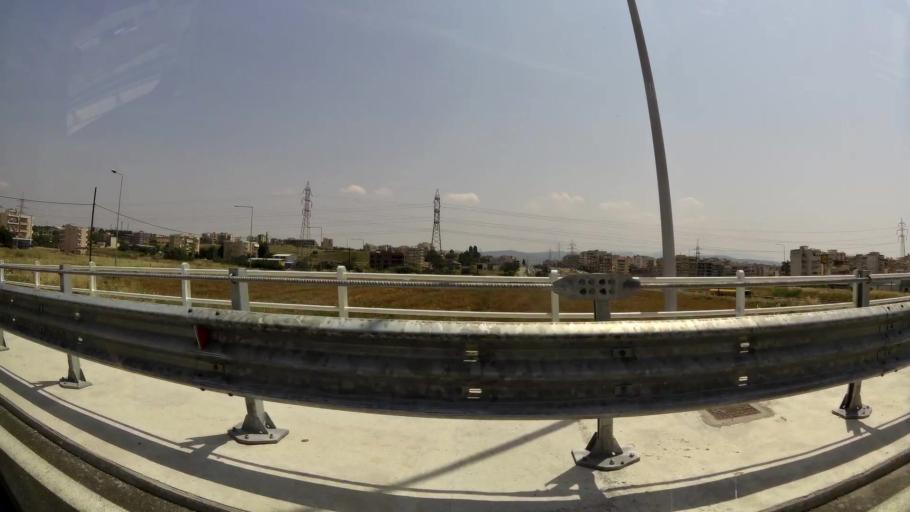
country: GR
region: Central Macedonia
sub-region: Nomos Thessalonikis
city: Evosmos
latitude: 40.6782
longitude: 22.8983
